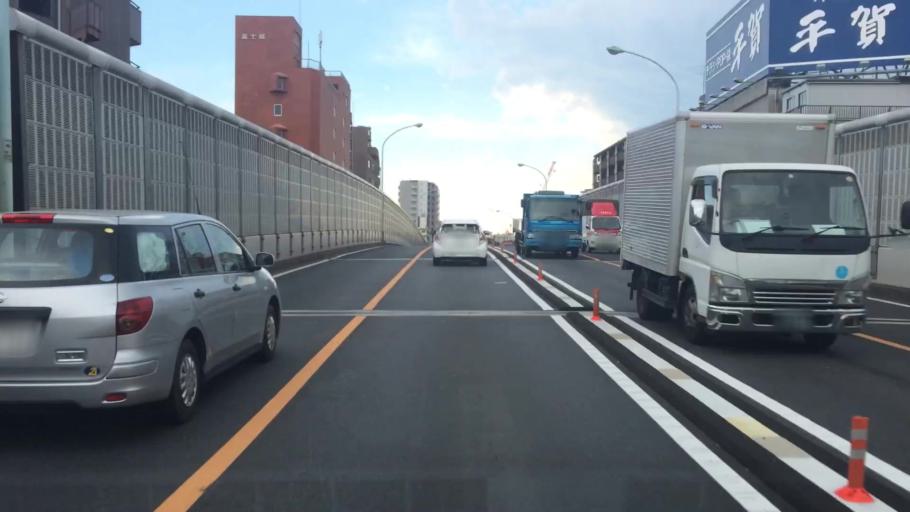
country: JP
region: Tokyo
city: Tokyo
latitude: 35.7354
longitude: 139.6632
